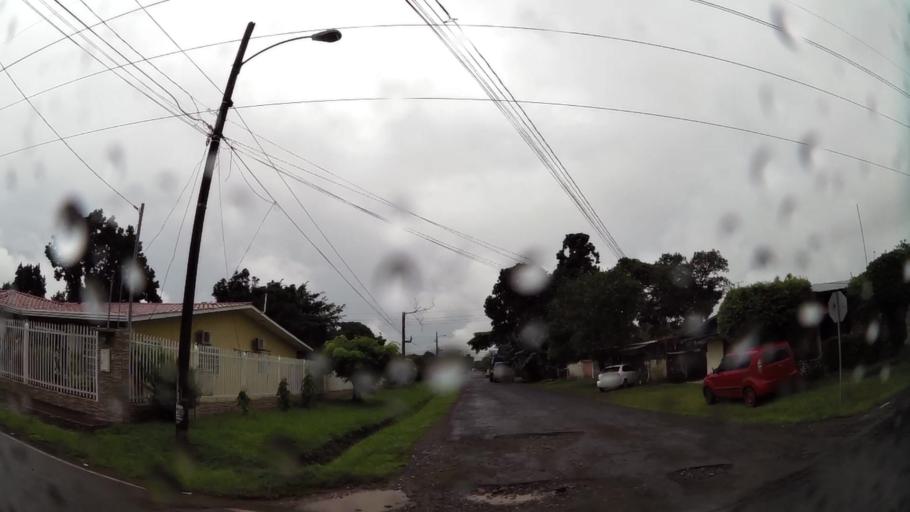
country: PA
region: Chiriqui
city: David
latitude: 8.4360
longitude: -82.4336
